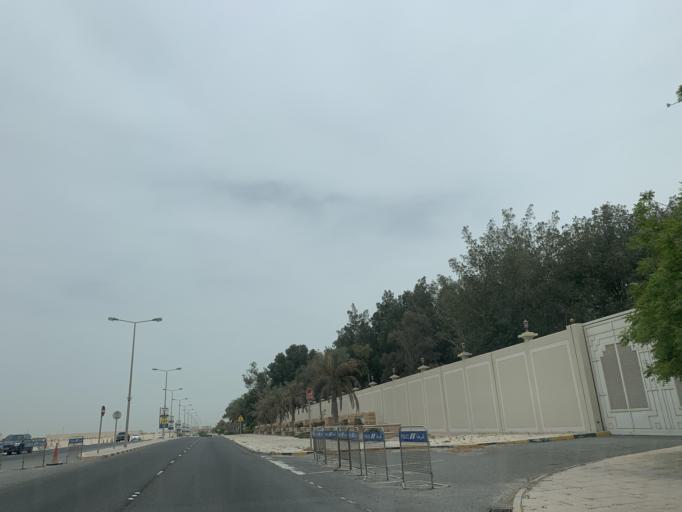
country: BH
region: Northern
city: Ar Rifa'
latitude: 26.1411
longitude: 50.5468
